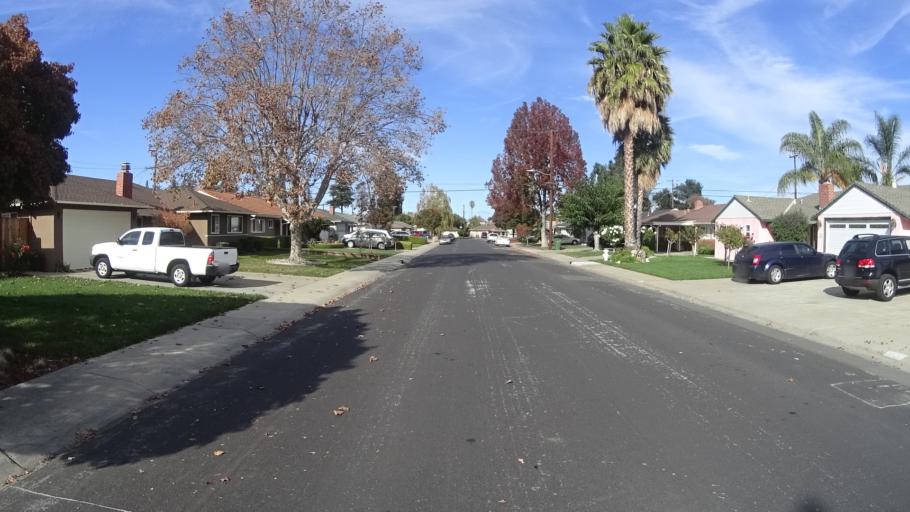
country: US
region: California
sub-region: Santa Clara County
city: Santa Clara
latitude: 37.3543
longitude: -121.9632
